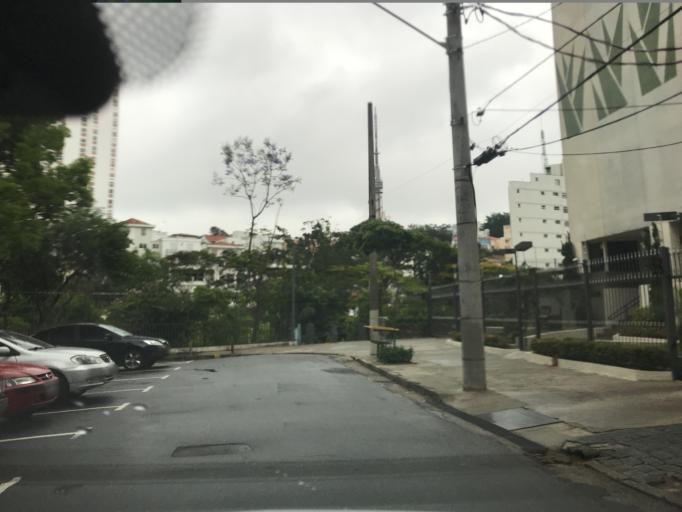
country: BR
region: Sao Paulo
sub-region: Sao Paulo
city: Sao Paulo
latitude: -23.5410
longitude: -46.6773
